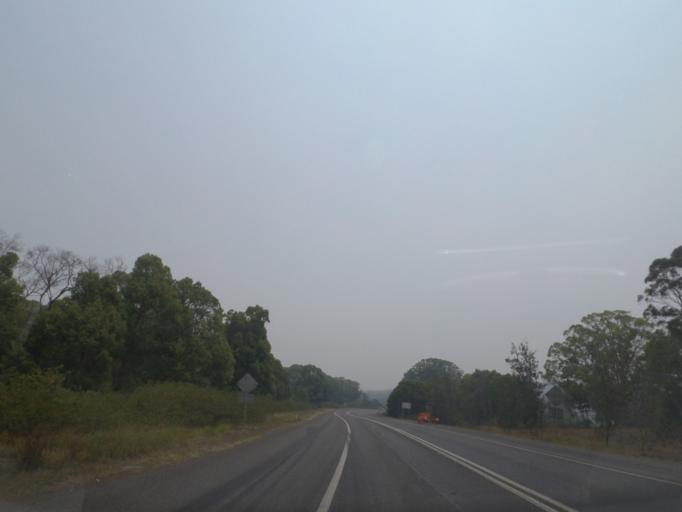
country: AU
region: New South Wales
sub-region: Clarence Valley
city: Maclean
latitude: -29.5473
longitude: 153.1560
